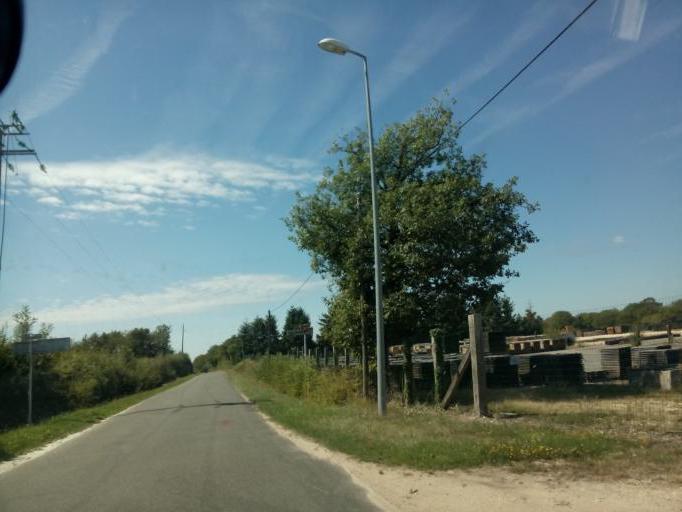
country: FR
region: Centre
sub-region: Departement du Cher
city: Neuvy-sur-Barangeon
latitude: 47.3090
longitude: 2.3561
